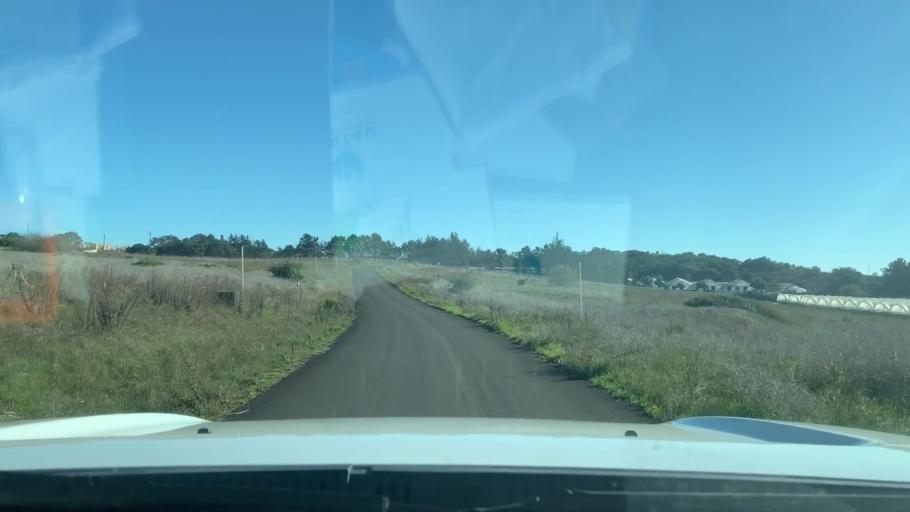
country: US
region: California
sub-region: San Luis Obispo County
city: Callender
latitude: 35.0655
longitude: -120.5647
